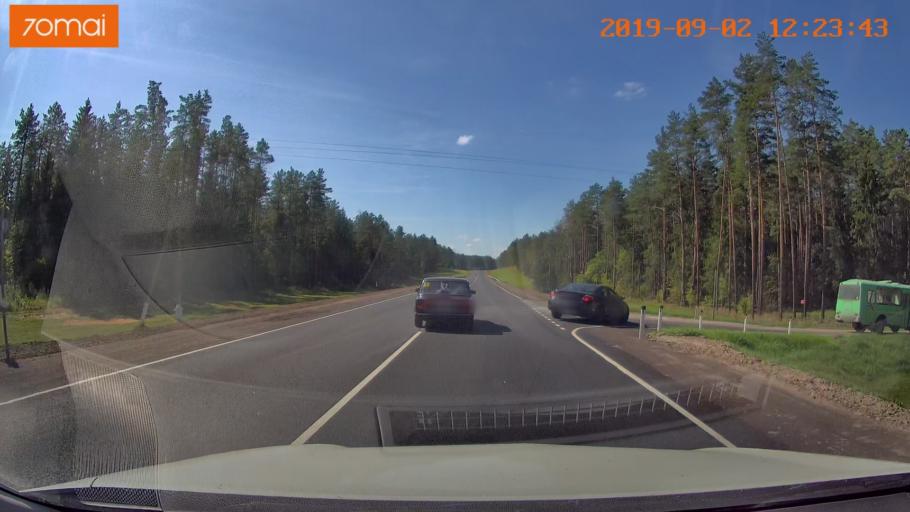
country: RU
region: Smolensk
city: Shumyachi
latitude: 53.8732
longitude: 32.6179
